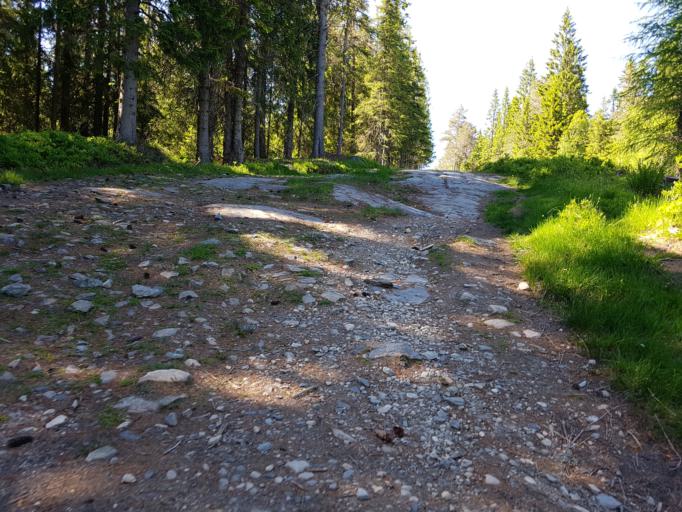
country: NO
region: Sor-Trondelag
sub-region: Trondheim
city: Trondheim
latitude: 63.4259
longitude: 10.2998
